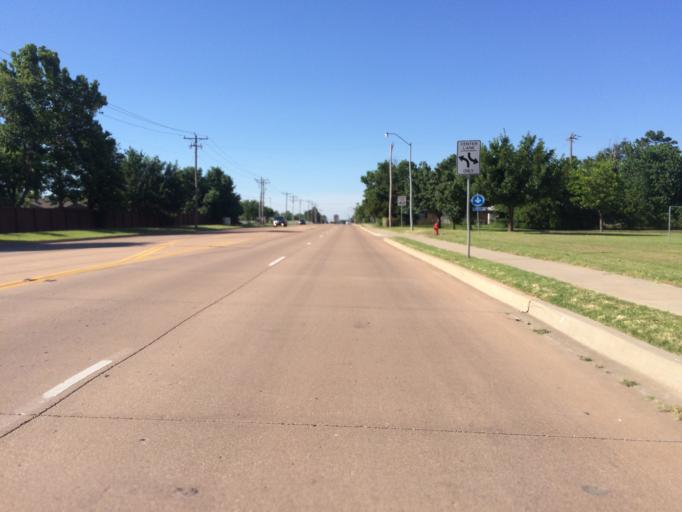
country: US
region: Oklahoma
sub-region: Cleveland County
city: Norman
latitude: 35.2387
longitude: -97.4413
